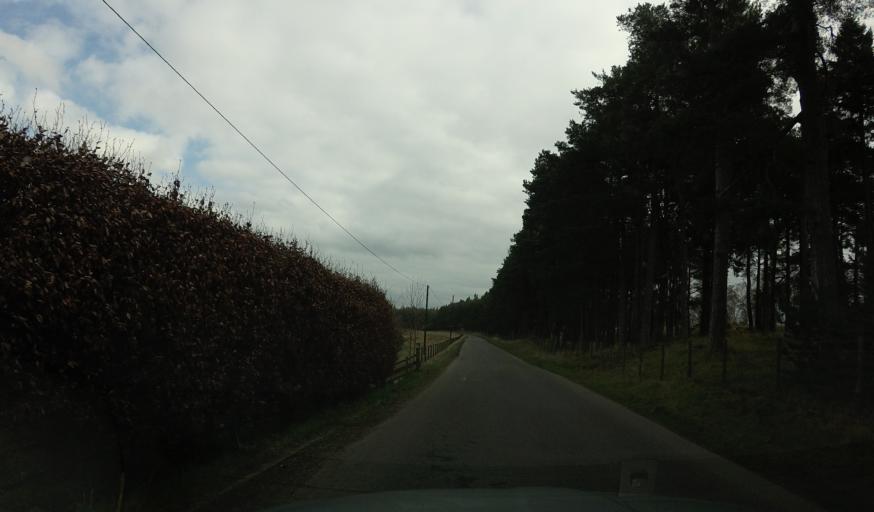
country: GB
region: Scotland
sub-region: Midlothian
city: Penicuik
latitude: 55.7678
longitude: -3.1392
